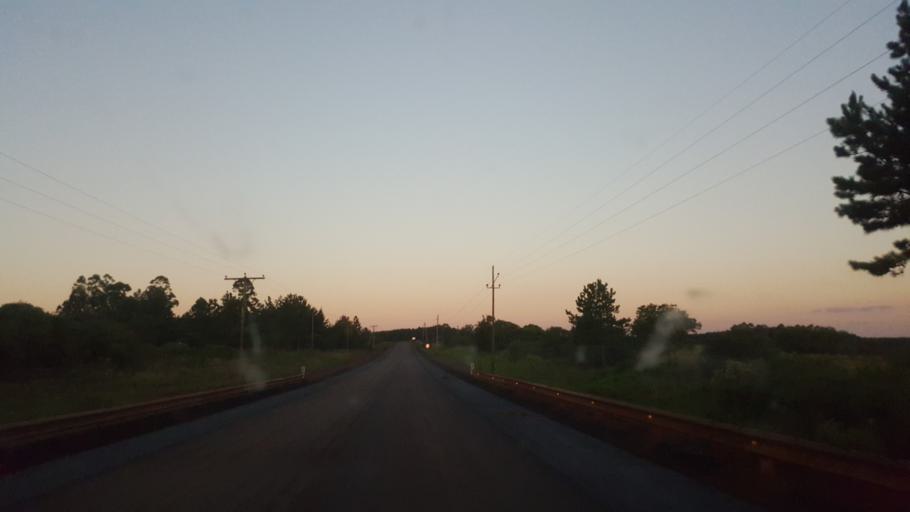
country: AR
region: Corrientes
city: Garruchos
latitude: -28.2311
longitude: -55.8096
